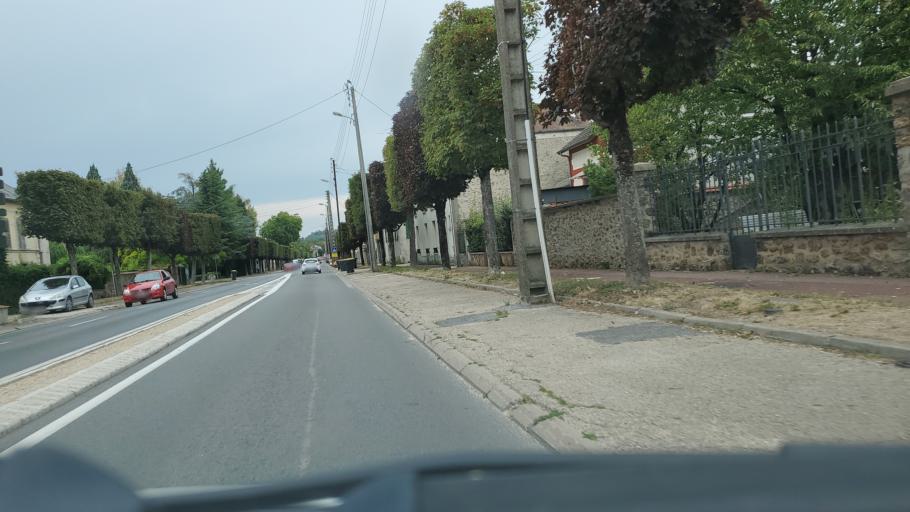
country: FR
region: Ile-de-France
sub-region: Departement de Seine-et-Marne
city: Coulommiers
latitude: 48.8038
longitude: 3.0854
